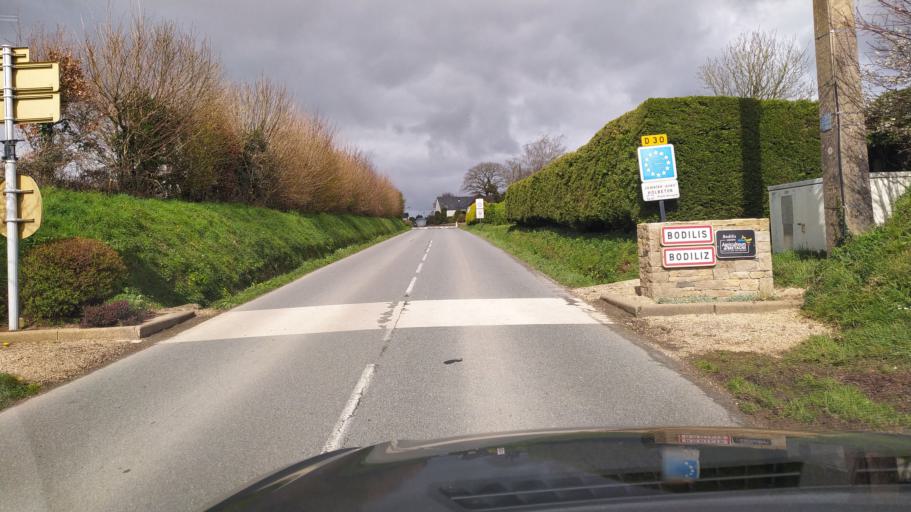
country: FR
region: Brittany
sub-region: Departement du Finistere
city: Bodilis
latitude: 48.5265
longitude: -4.1170
